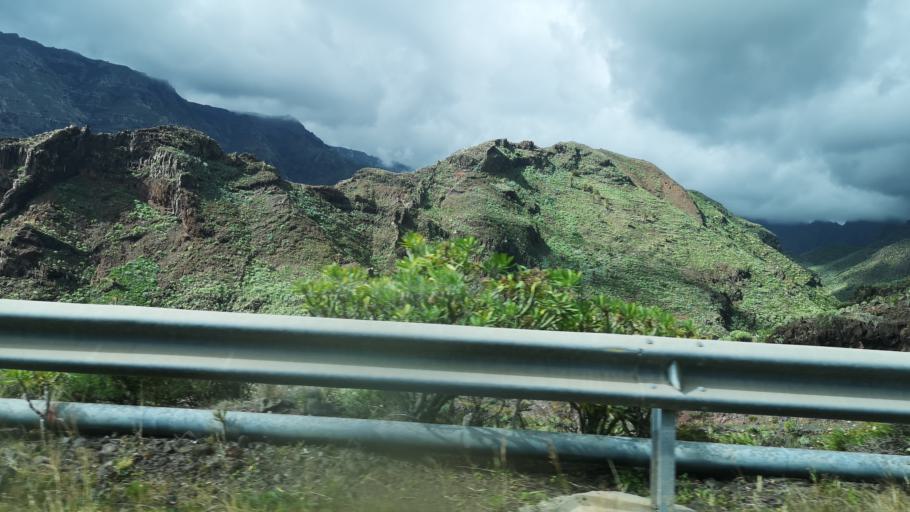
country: ES
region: Canary Islands
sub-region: Provincia de Santa Cruz de Tenerife
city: San Sebastian de la Gomera
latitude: 28.1157
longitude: -17.1387
